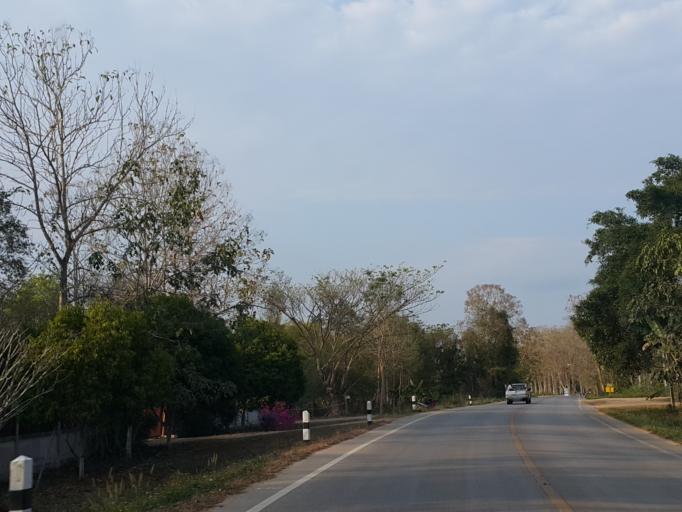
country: TH
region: Lampang
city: Chae Hom
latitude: 18.5237
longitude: 99.4769
